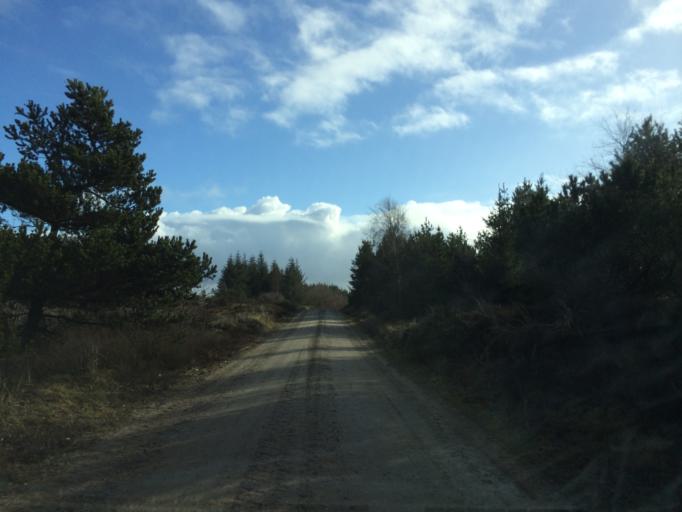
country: DK
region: Central Jutland
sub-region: Holstebro Kommune
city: Ulfborg
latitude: 56.2774
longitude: 8.3688
